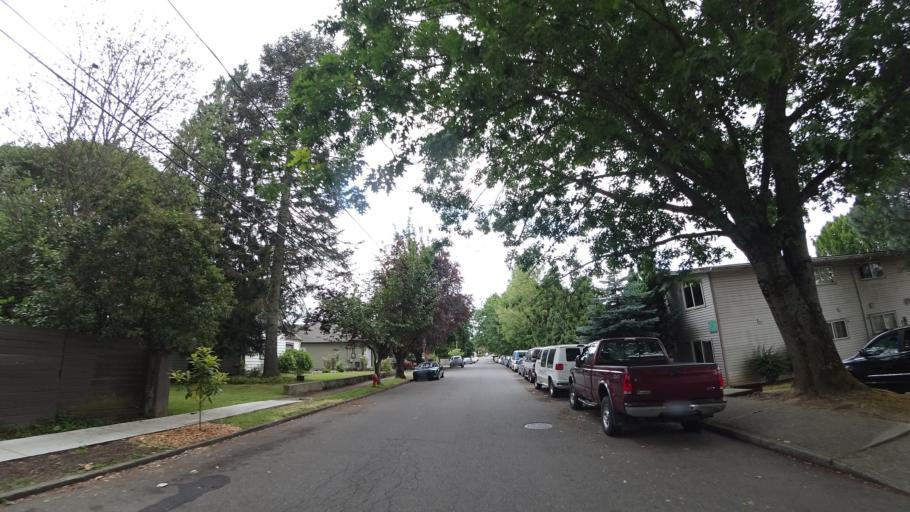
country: US
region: Oregon
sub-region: Multnomah County
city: Lents
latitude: 45.5614
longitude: -122.5931
